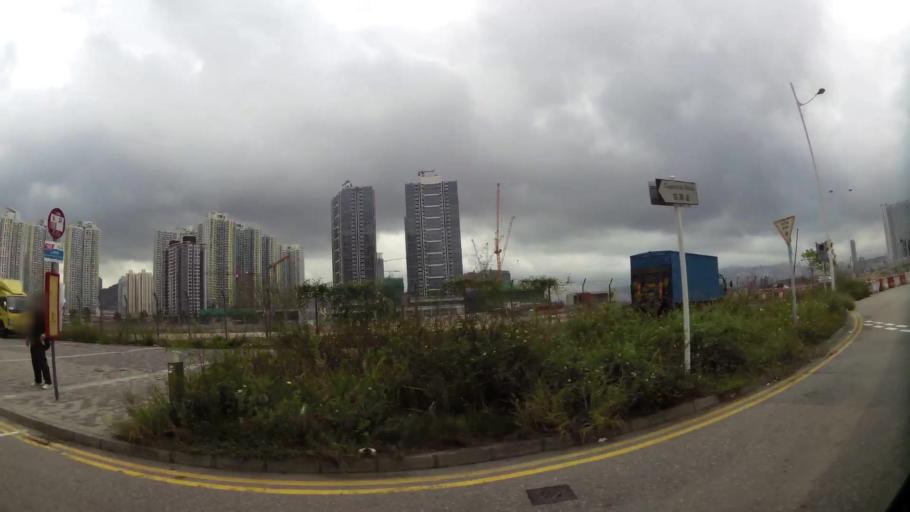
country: HK
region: Kowloon City
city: Kowloon
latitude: 22.3316
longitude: 114.1975
